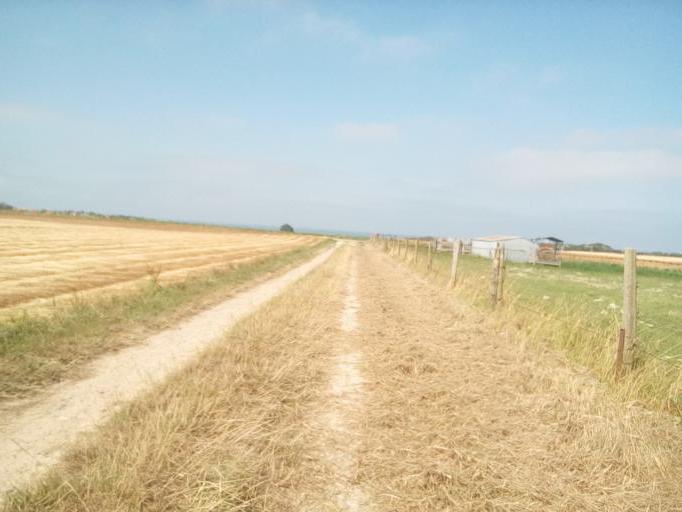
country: FR
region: Lower Normandy
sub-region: Departement du Calvados
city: Bernieres-sur-Mer
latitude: 49.3149
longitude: -0.4390
